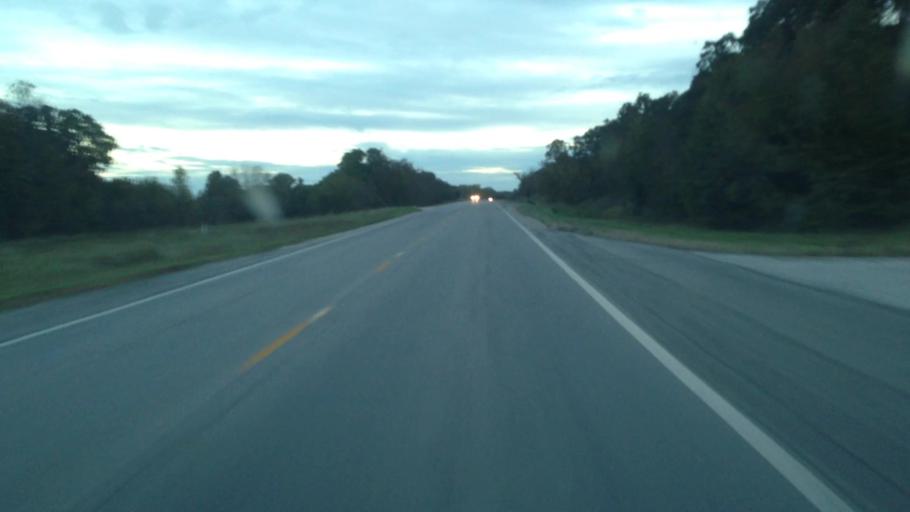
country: US
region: Kansas
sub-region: Anderson County
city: Garnett
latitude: 38.2093
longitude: -95.2490
